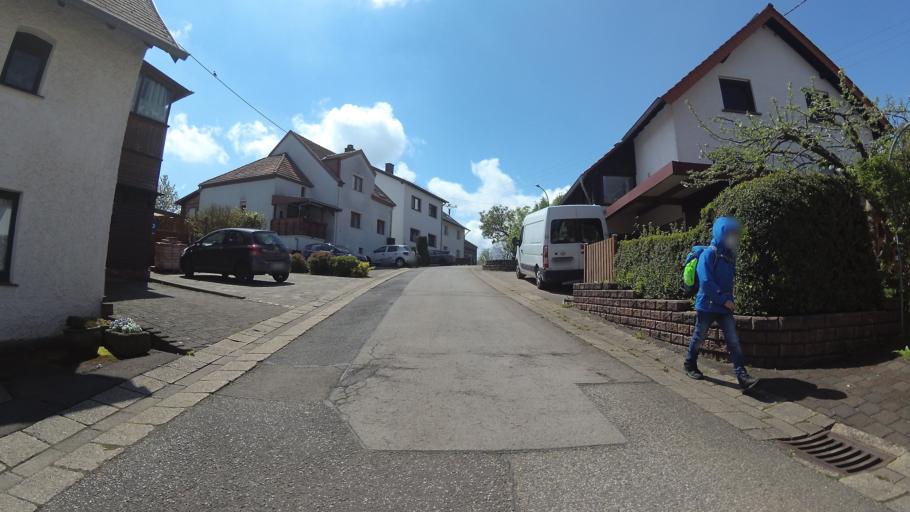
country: DE
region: Saarland
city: Illingen
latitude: 49.3955
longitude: 7.0365
